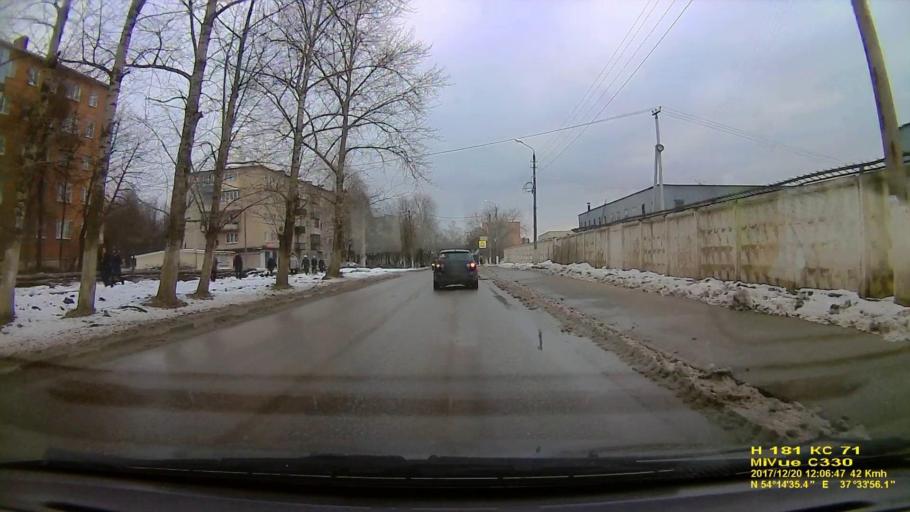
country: RU
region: Tula
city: Gorelki
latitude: 54.2432
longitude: 37.5656
